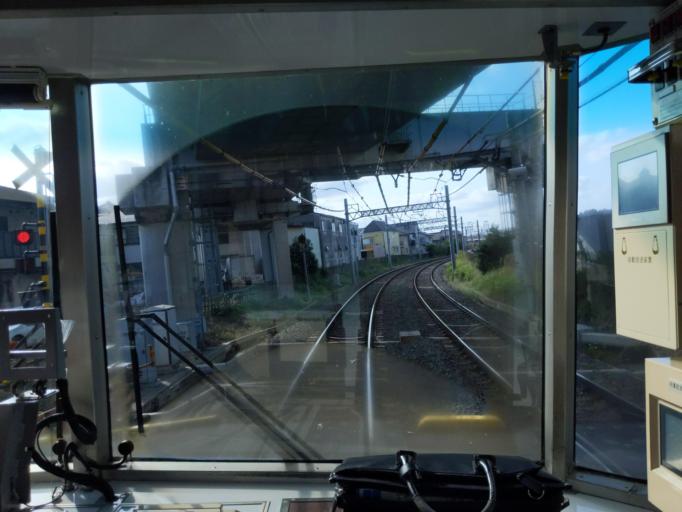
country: JP
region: Chiba
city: Kashiwa
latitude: 35.7762
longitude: 139.9865
